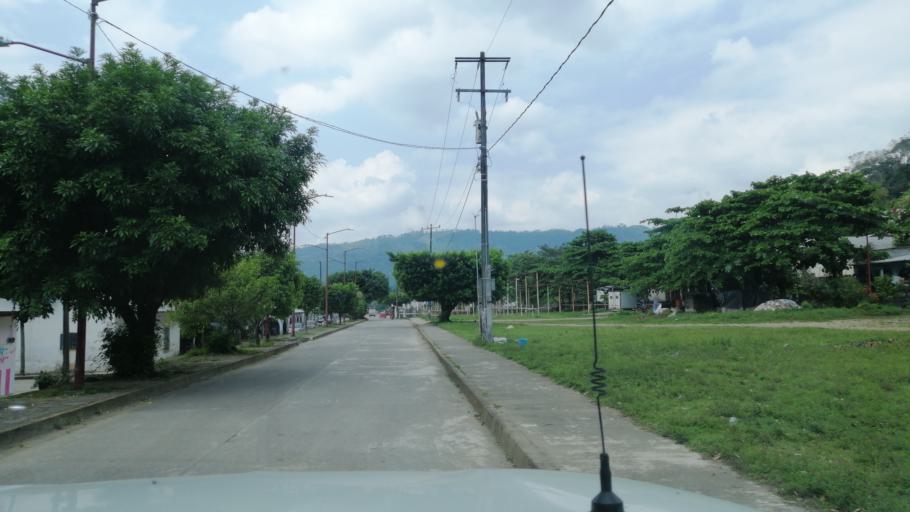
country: MX
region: Chiapas
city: Ostuacan
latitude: 17.4052
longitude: -93.3343
